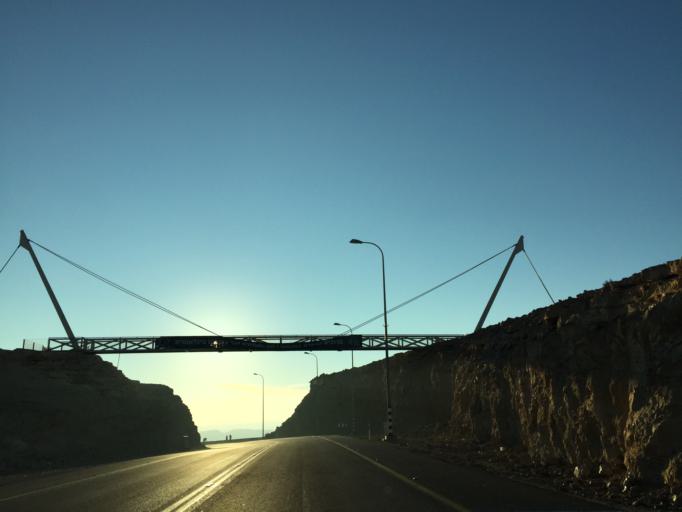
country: IL
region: Southern District
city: Mitzpe Ramon
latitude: 30.6103
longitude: 34.8063
